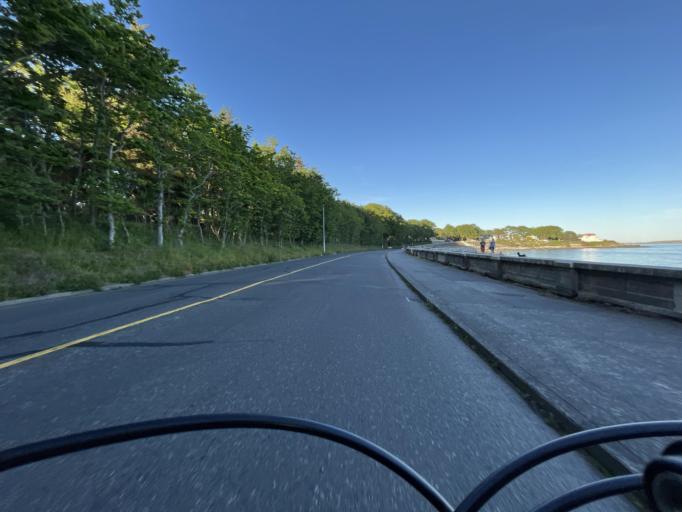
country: CA
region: British Columbia
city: Victoria
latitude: 48.4101
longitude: -123.3408
